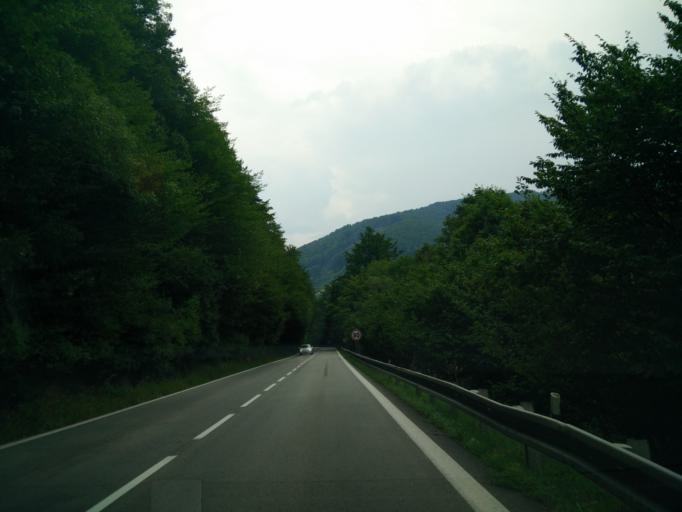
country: SK
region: Nitriansky
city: Handlova
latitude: 48.6602
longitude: 18.7330
